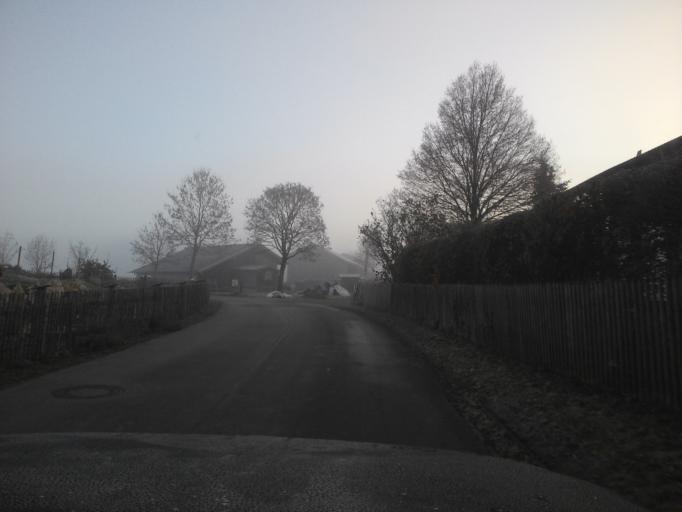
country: DE
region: Bavaria
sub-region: Upper Bavaria
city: Bernried
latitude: 47.8367
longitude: 11.2403
